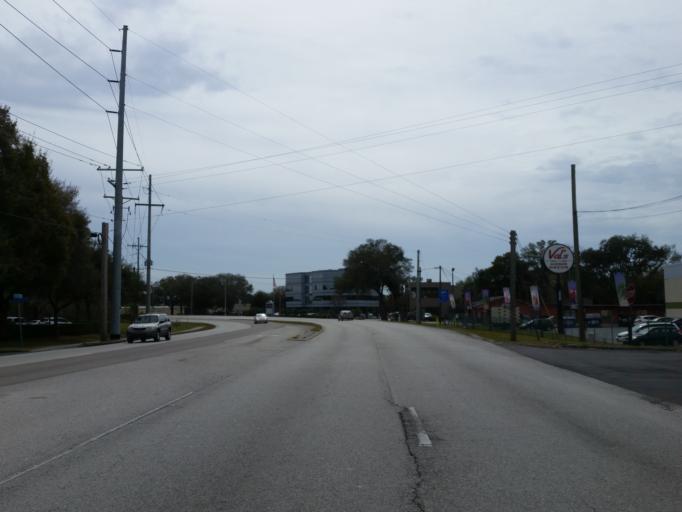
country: US
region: Florida
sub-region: Hillsborough County
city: Carrollwood
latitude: 28.0386
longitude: -82.5082
